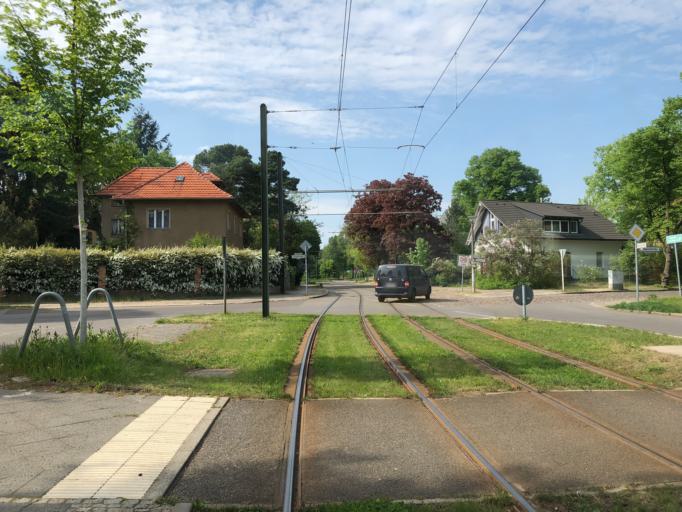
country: DE
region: Berlin
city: Schmockwitz
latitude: 52.3948
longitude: 13.6316
